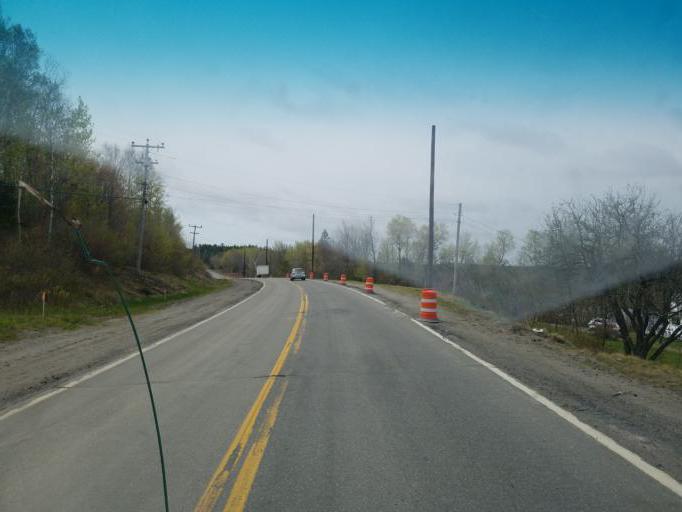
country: US
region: Maine
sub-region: Washington County
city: East Machias
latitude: 44.7806
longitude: -67.1945
